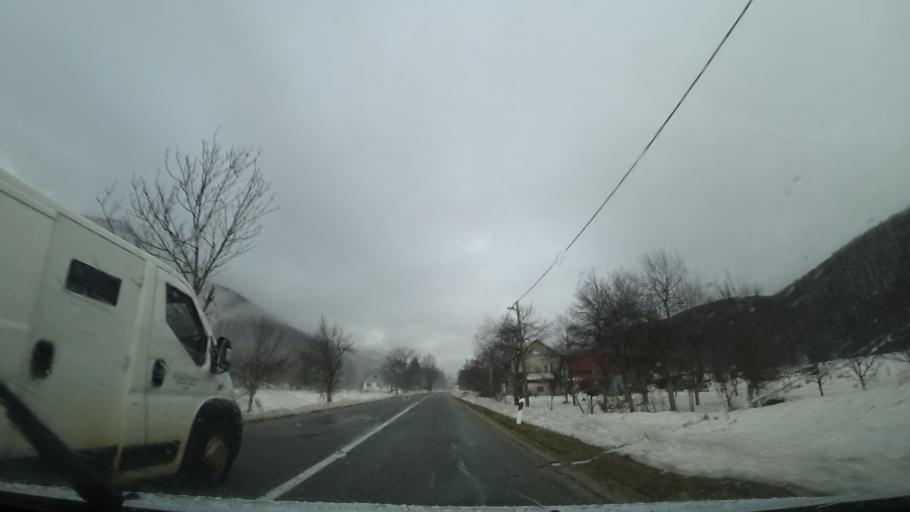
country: HR
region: Licko-Senjska
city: Gospic
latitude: 44.5032
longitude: 15.2625
